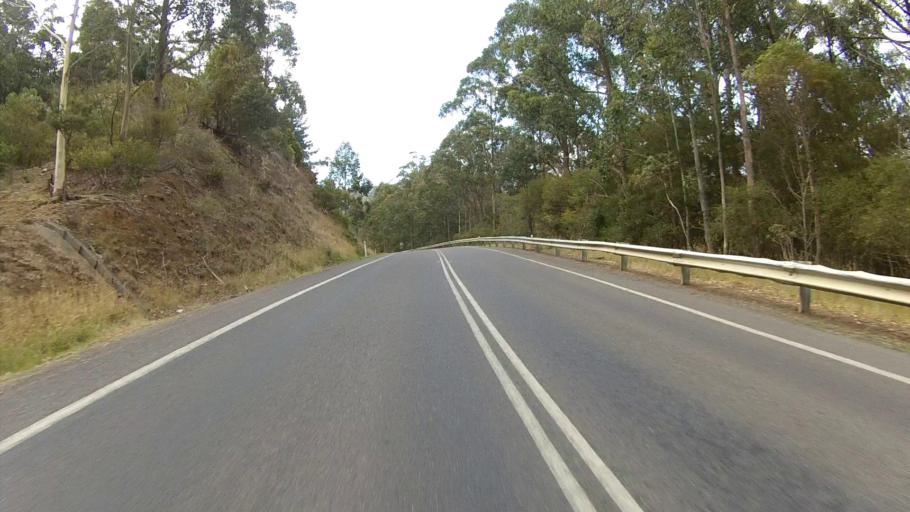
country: AU
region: Tasmania
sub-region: Kingborough
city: Kettering
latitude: -43.1016
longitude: 147.2445
